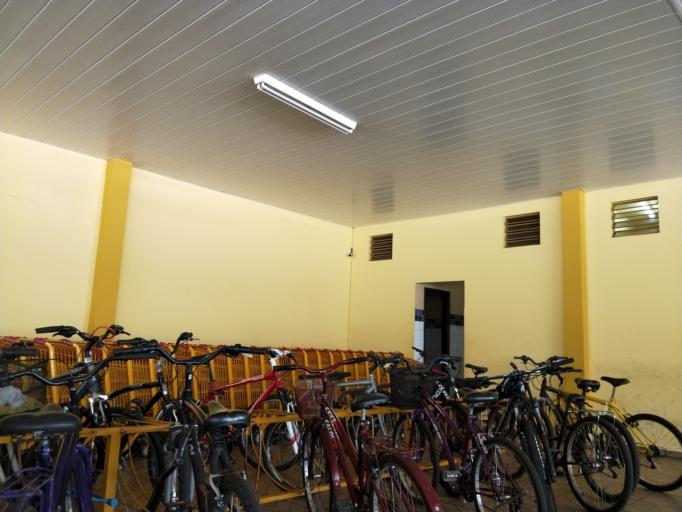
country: BR
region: Parana
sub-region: Marechal Candido Rondon
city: Marechal Candido Rondon
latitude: -24.5666
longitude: -54.0574
